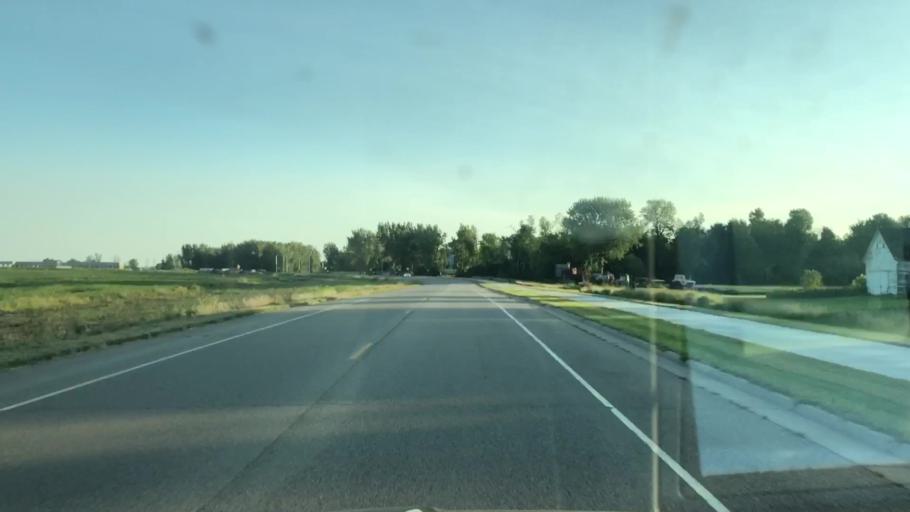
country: US
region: Minnesota
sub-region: Nobles County
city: Worthington
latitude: 43.6179
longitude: -95.6348
